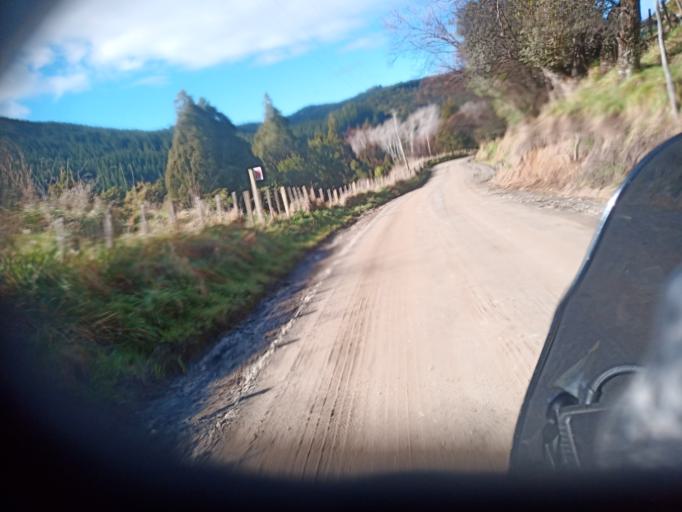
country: NZ
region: Gisborne
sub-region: Gisborne District
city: Gisborne
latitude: -38.0463
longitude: 178.1193
